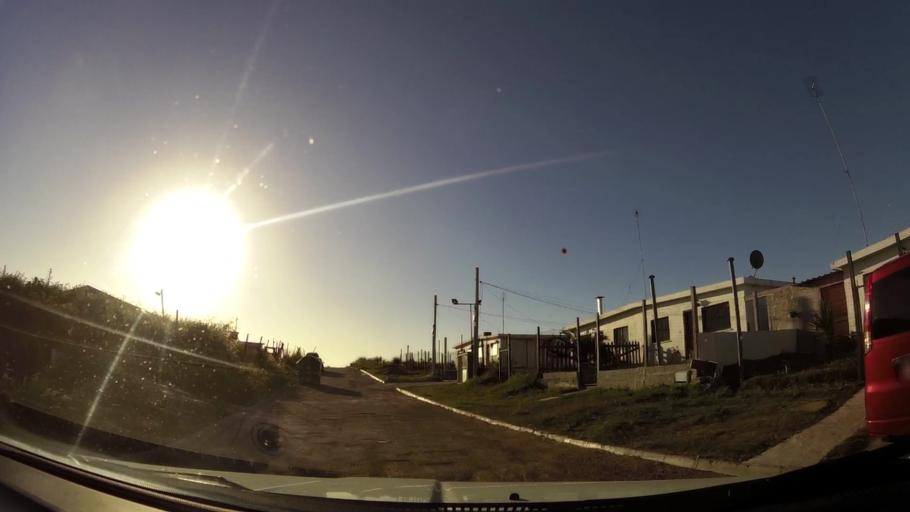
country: UY
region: Canelones
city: La Paz
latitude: -34.8292
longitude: -56.2333
